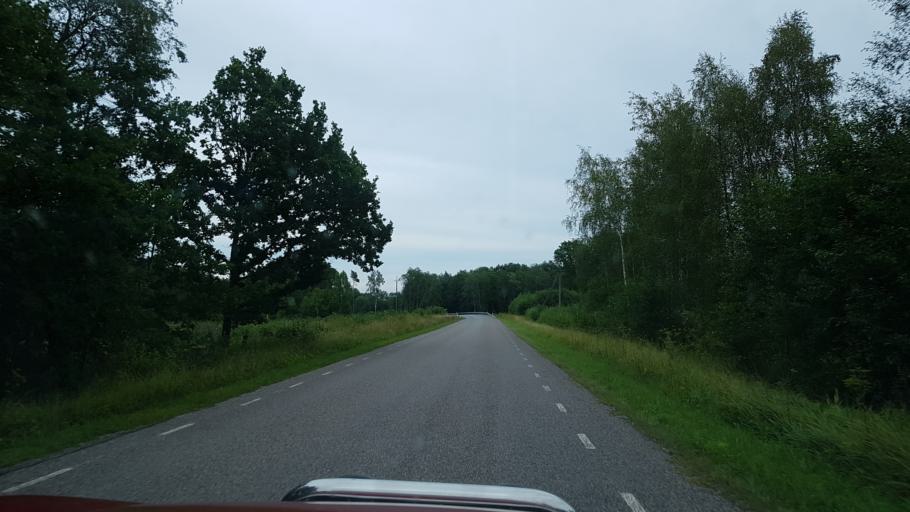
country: EE
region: Laeaene
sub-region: Lihula vald
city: Lihula
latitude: 58.8785
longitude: 23.8174
